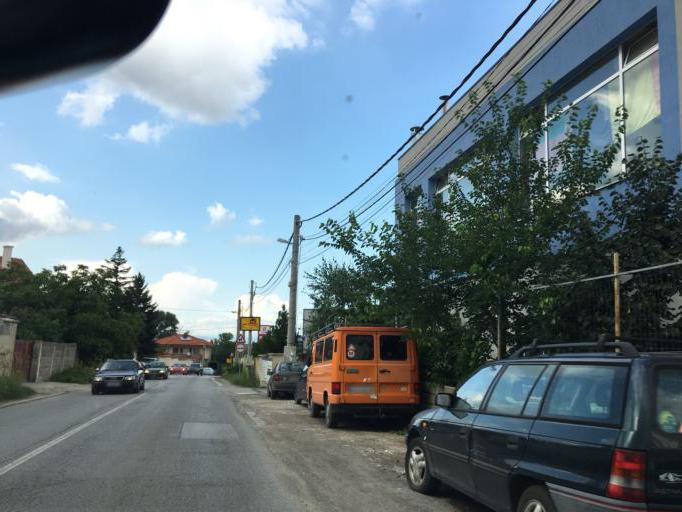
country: BG
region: Sofia-Capital
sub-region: Stolichna Obshtina
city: Sofia
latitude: 42.6383
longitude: 23.3533
